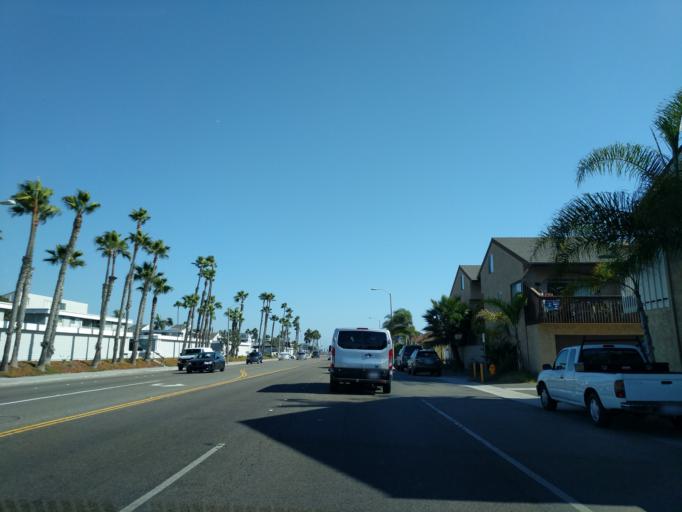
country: US
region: California
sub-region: Orange County
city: Seal Beach
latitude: 33.7140
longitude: -118.0659
